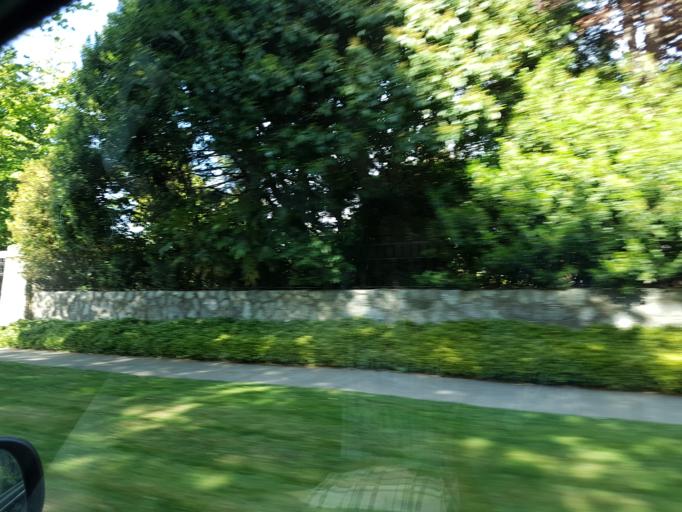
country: CA
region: British Columbia
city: Oak Bay
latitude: 48.4444
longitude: -123.2933
